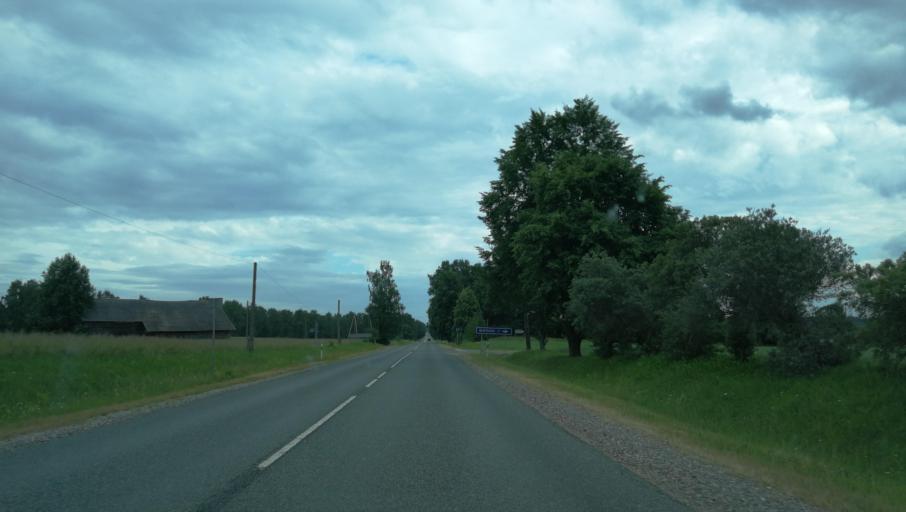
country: LV
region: Naukseni
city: Naukseni
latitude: 57.7200
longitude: 25.4232
